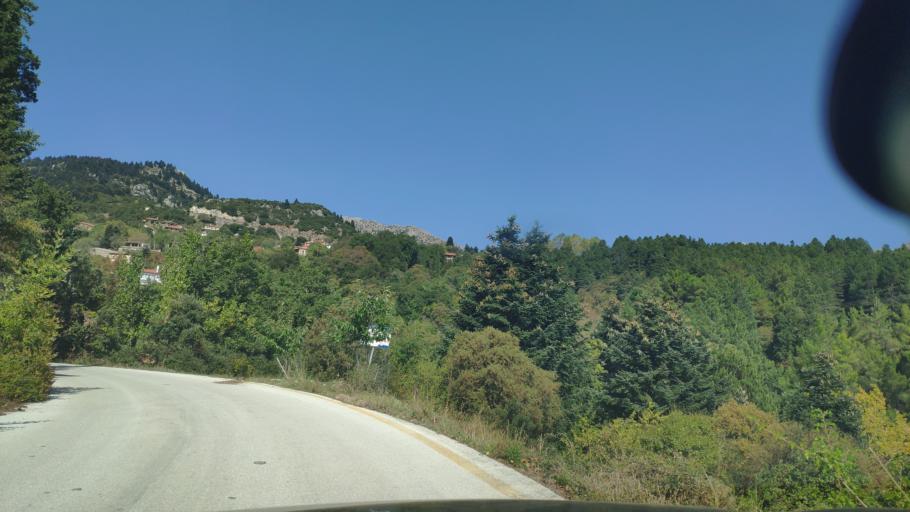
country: GR
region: Peloponnese
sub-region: Nomos Korinthias
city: Nemea
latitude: 37.8639
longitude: 22.3860
